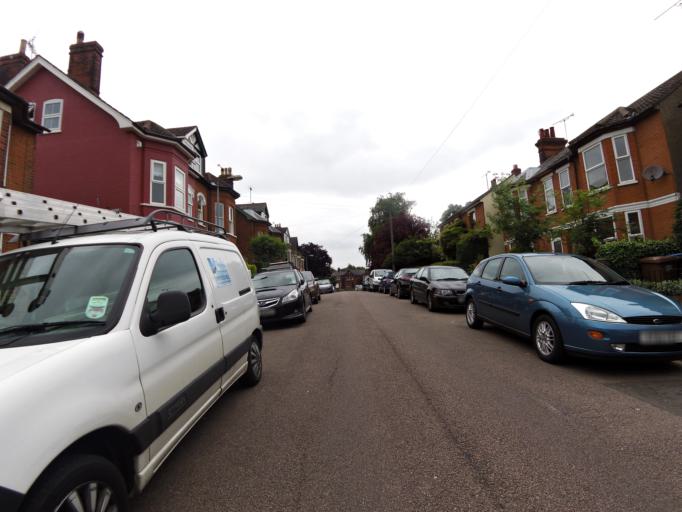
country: GB
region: England
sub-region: Suffolk
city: Ipswich
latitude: 52.0490
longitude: 1.1495
